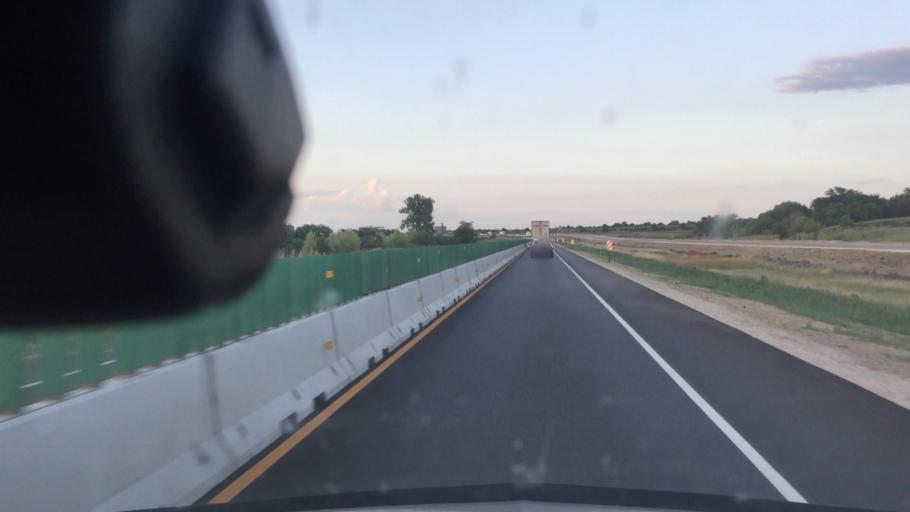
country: US
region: Illinois
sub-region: Livingston County
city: Pontiac
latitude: 40.9448
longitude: -88.5868
